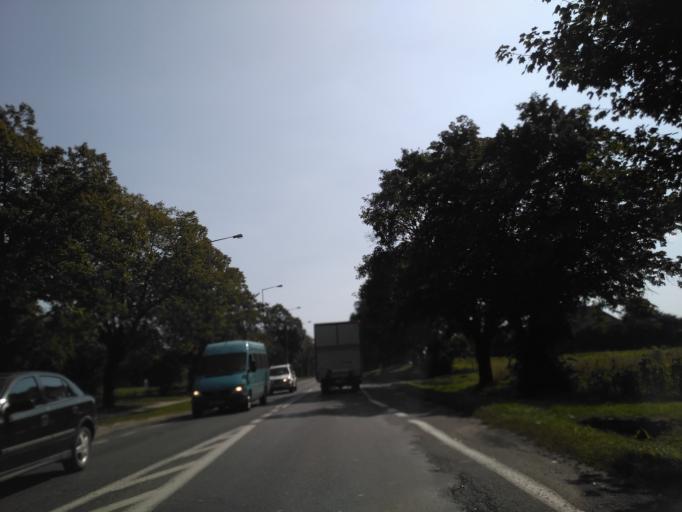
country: PL
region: Lublin Voivodeship
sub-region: Powiat lubelski
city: Lublin
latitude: 51.1915
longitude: 22.5856
